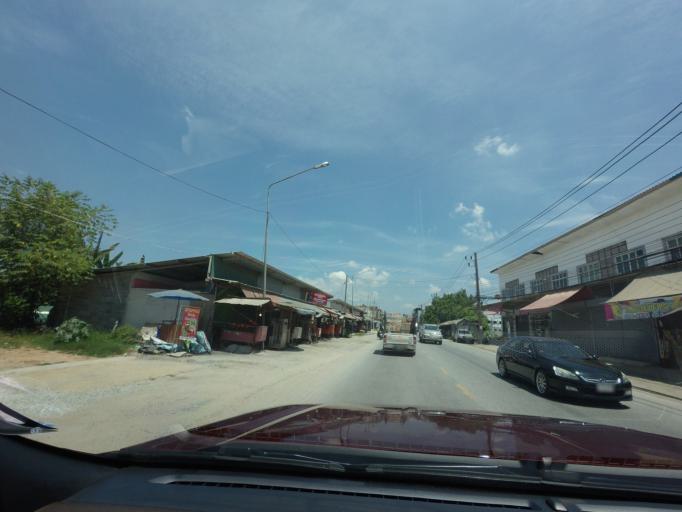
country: TH
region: Yala
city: Yala
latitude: 6.5567
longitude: 101.2736
